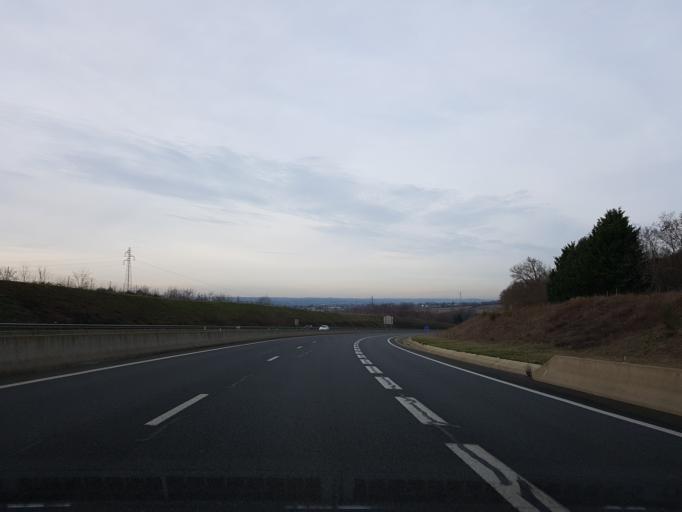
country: FR
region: Auvergne
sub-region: Departement de l'Allier
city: Desertines
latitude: 46.3708
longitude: 2.6306
